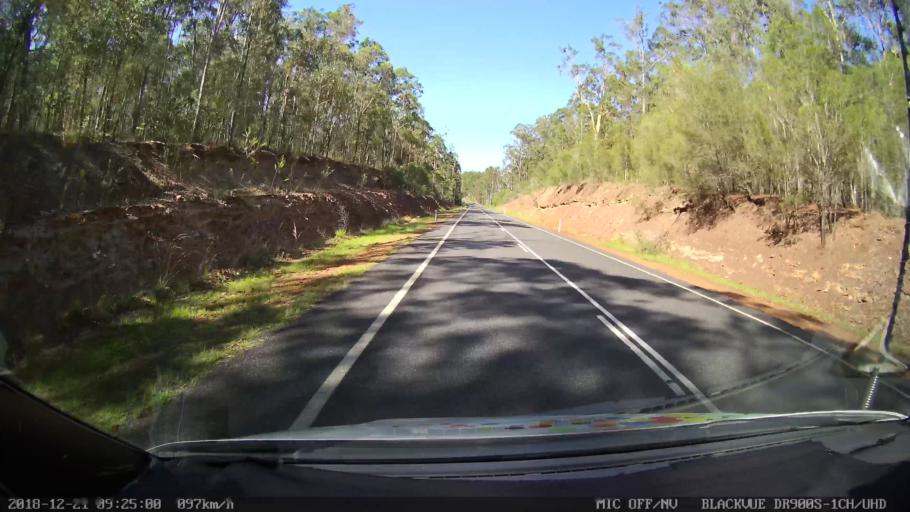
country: AU
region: New South Wales
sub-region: Clarence Valley
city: Maclean
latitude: -29.3742
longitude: 153.0124
